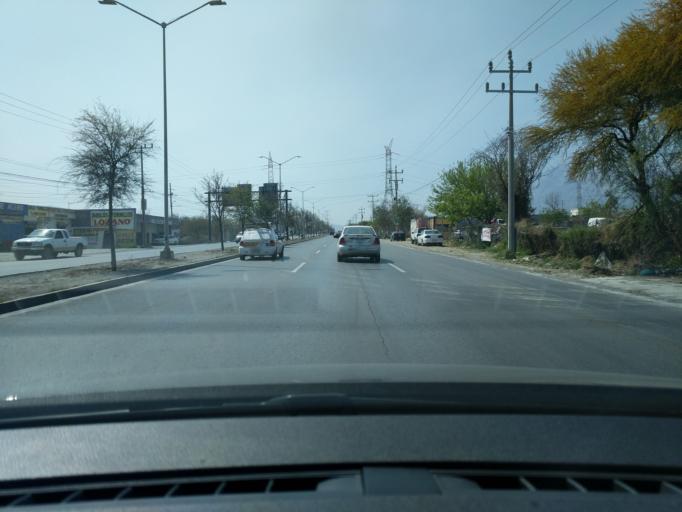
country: MX
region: Nuevo Leon
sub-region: Garcia
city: Valle de Lincoln
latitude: 25.7899
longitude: -100.4988
